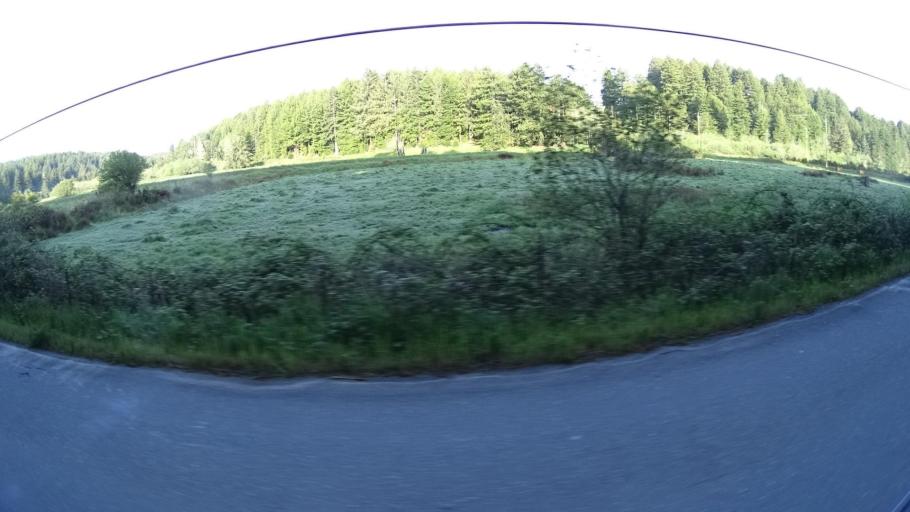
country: US
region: California
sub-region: Humboldt County
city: Myrtletown
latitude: 40.7797
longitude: -124.1183
